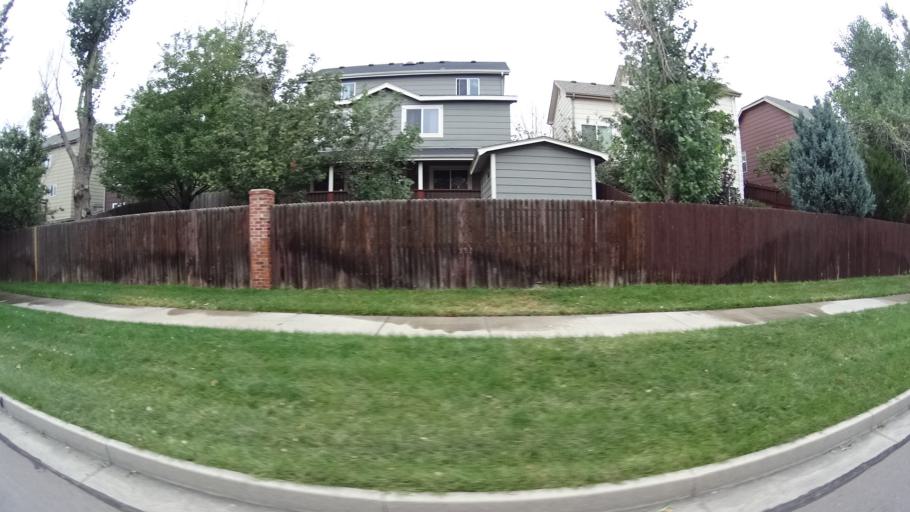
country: US
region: Colorado
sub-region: El Paso County
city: Cimarron Hills
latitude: 38.9012
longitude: -104.7099
